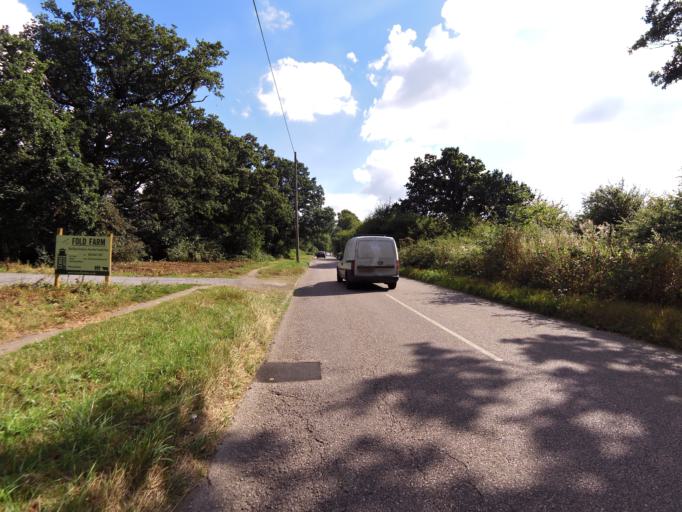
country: GB
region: England
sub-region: Greater London
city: High Barnet
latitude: 51.6617
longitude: -0.2293
